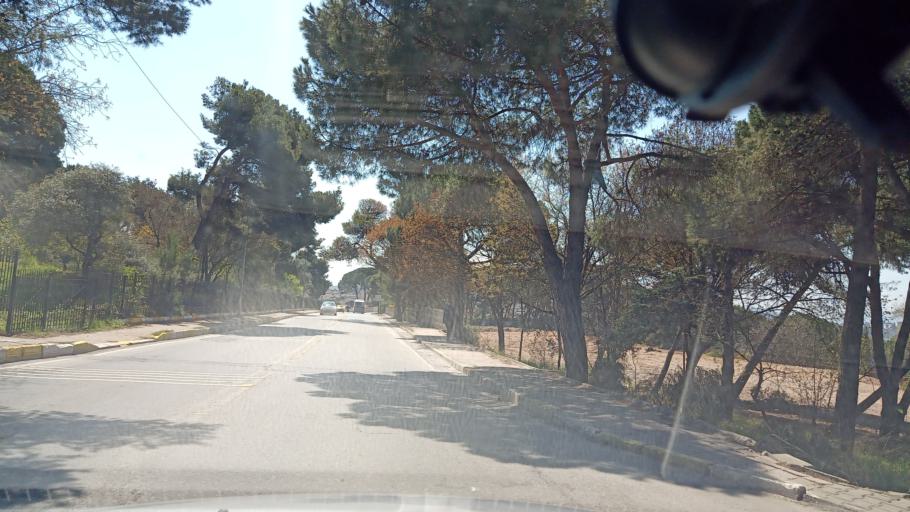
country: TR
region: Istanbul
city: Maltepe
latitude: 40.9502
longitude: 29.1423
